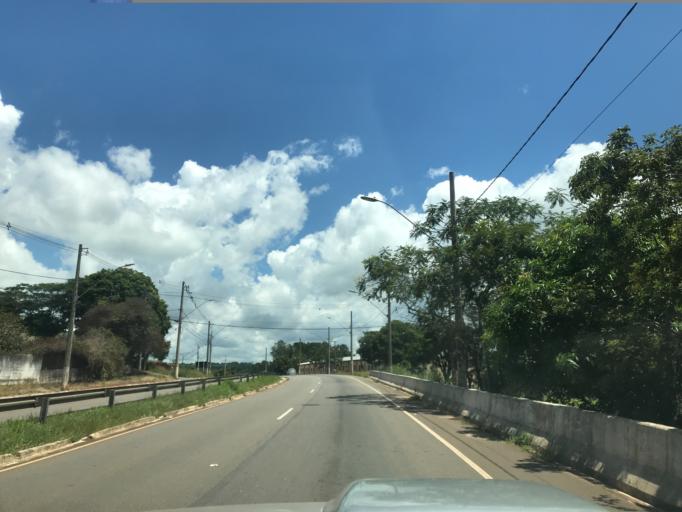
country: BR
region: Minas Gerais
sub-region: Tres Coracoes
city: Tres Coracoes
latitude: -21.6675
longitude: -45.2740
